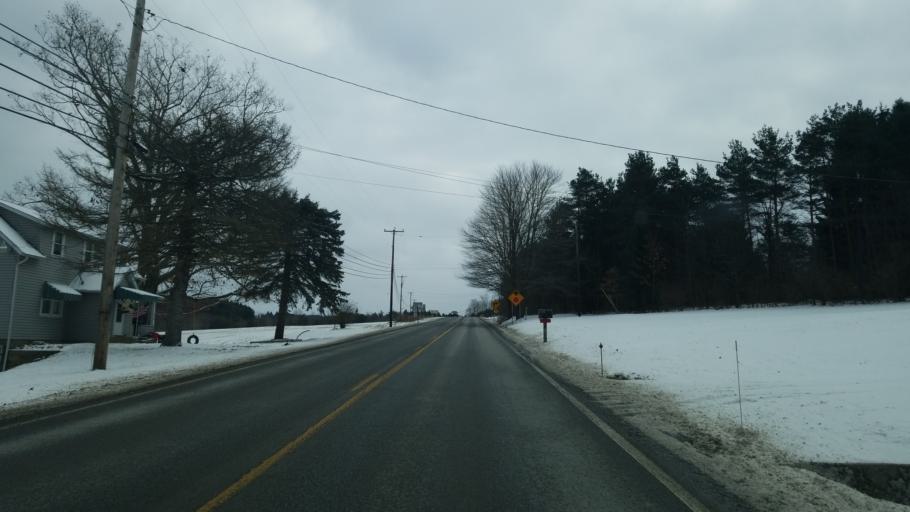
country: US
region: Pennsylvania
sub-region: Clearfield County
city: Sandy
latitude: 41.0818
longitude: -78.7610
